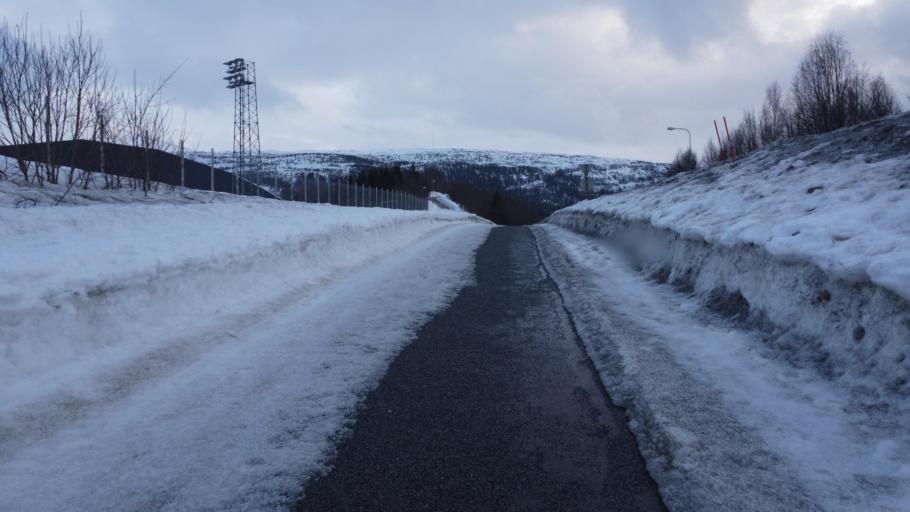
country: NO
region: Nordland
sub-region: Rana
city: Mo i Rana
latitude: 66.3236
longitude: 14.1582
